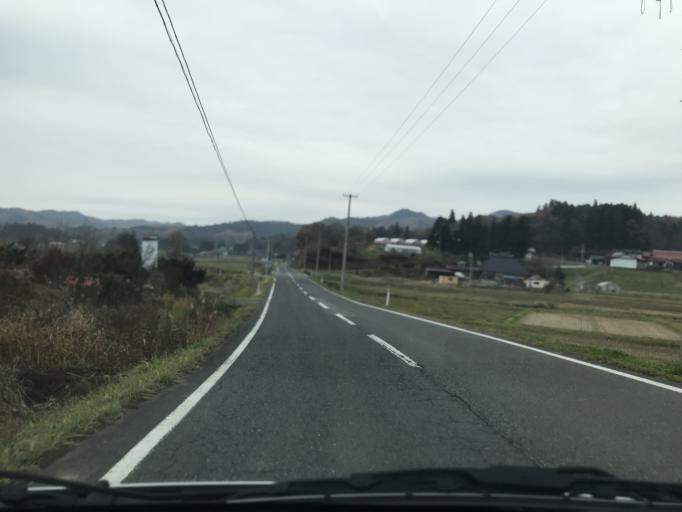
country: JP
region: Iwate
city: Kitakami
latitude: 39.2572
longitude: 141.2043
